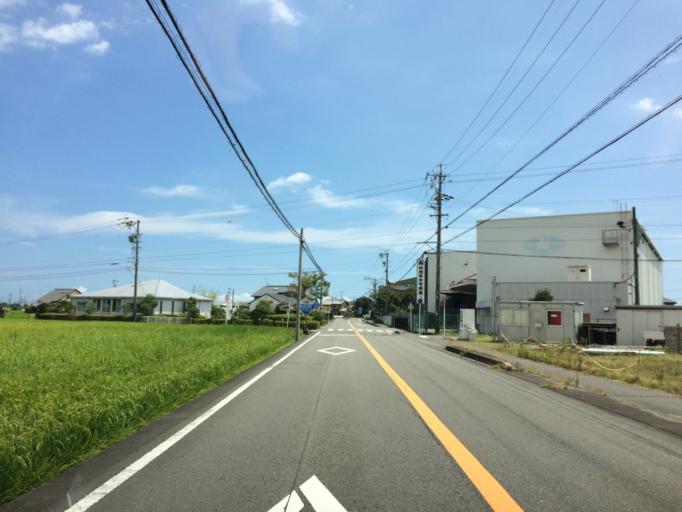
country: JP
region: Shizuoka
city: Yaizu
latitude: 34.8868
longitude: 138.3124
